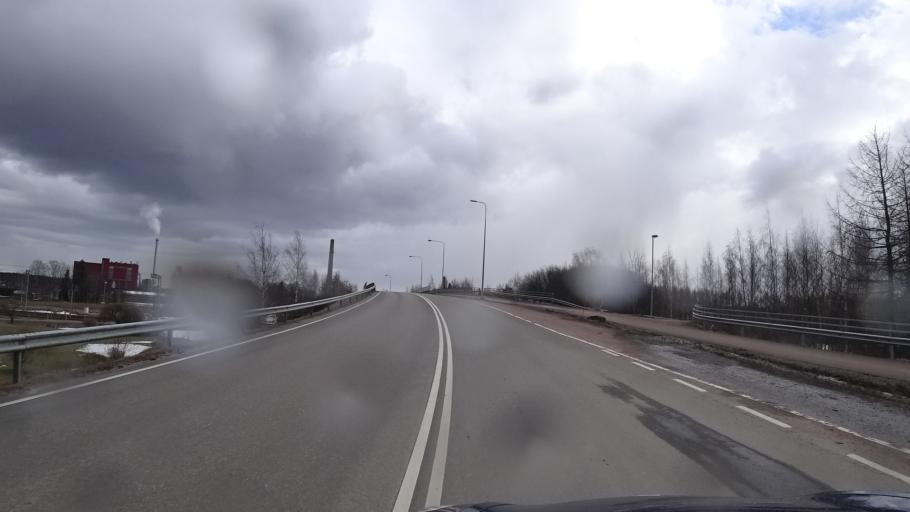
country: FI
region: Kymenlaakso
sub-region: Kotka-Hamina
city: Karhula
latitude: 60.5379
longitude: 26.9030
